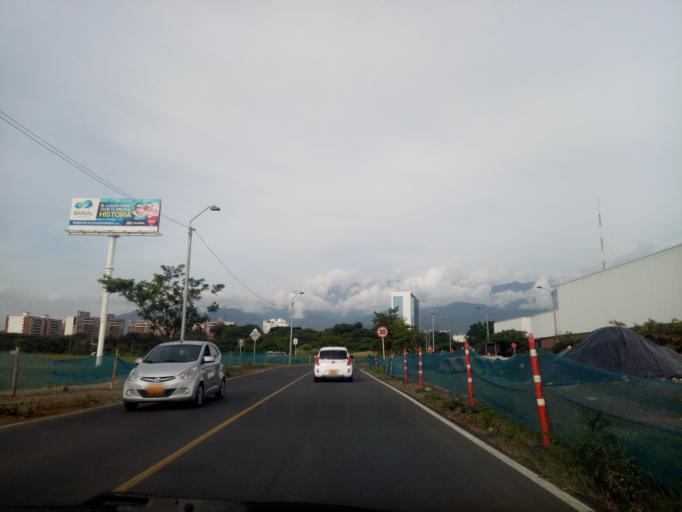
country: CO
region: Valle del Cauca
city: Cali
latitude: 3.3677
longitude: -76.5226
